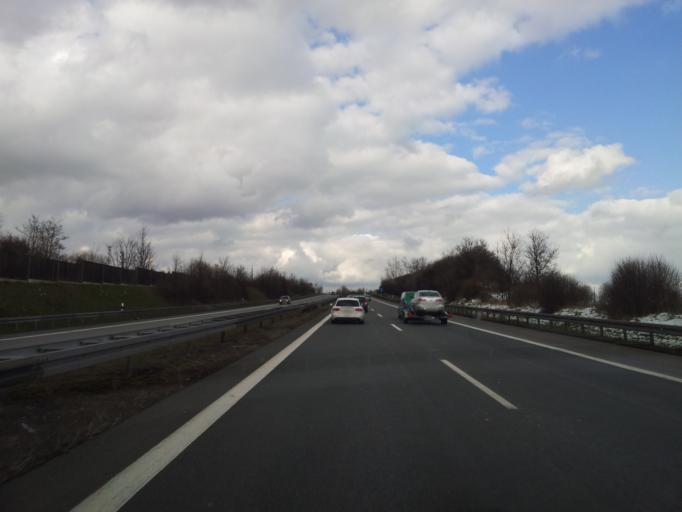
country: DE
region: Saxony
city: Hirschfeld
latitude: 50.6331
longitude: 12.4290
